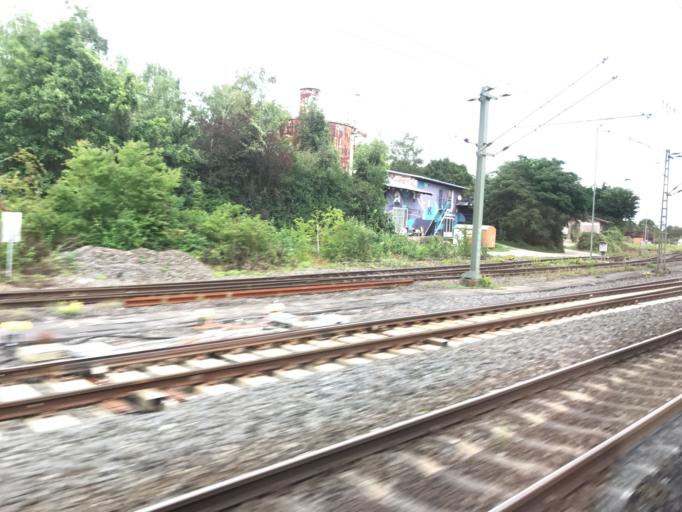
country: DE
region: Hesse
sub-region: Regierungsbezirk Giessen
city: Limburg an der Lahn
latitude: 50.3767
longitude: 8.0490
